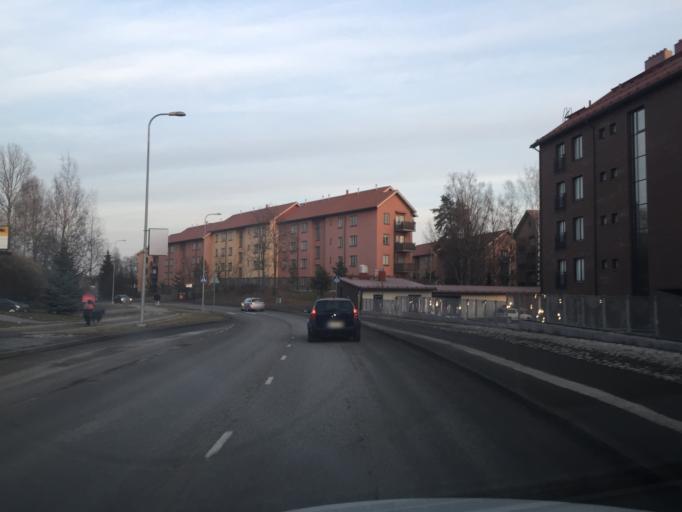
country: FI
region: Uusimaa
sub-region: Helsinki
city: Vantaa
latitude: 60.2845
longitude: 24.9648
